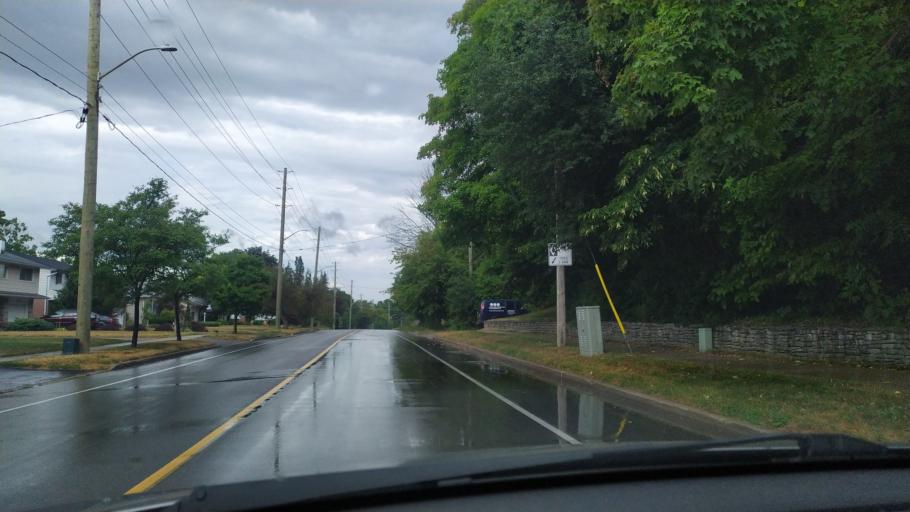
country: CA
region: Ontario
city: Waterloo
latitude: 43.4765
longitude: -80.5091
